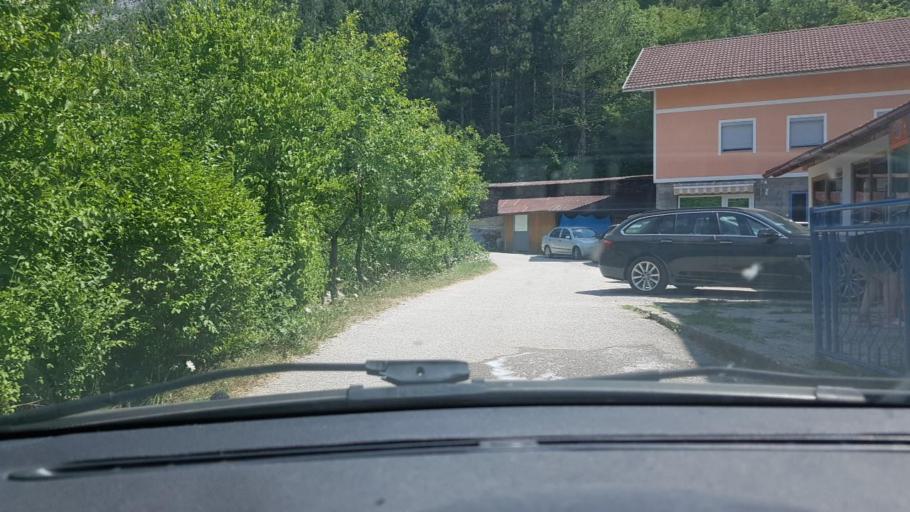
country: BA
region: Federation of Bosnia and Herzegovina
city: Orasac
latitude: 44.4898
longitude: 16.1436
